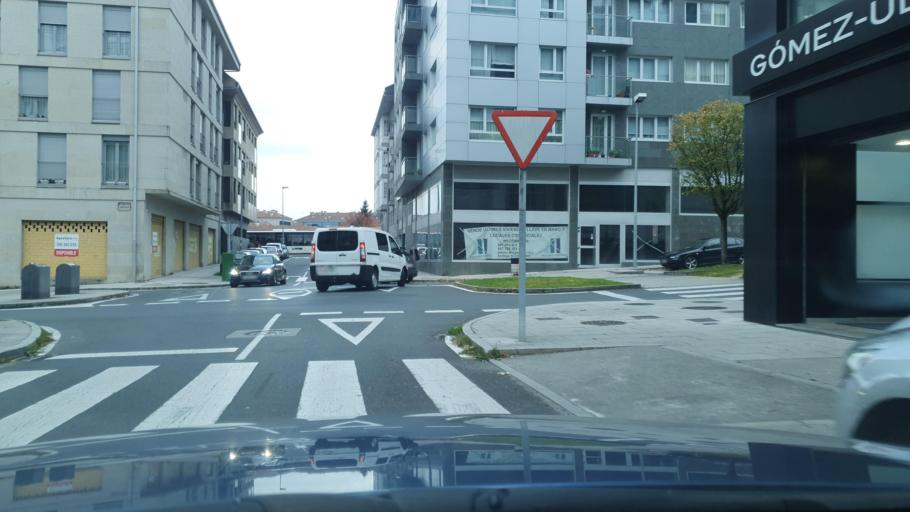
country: ES
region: Galicia
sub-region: Provincia da Coruna
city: Santiago de Compostela
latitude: 42.8682
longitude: -8.5597
